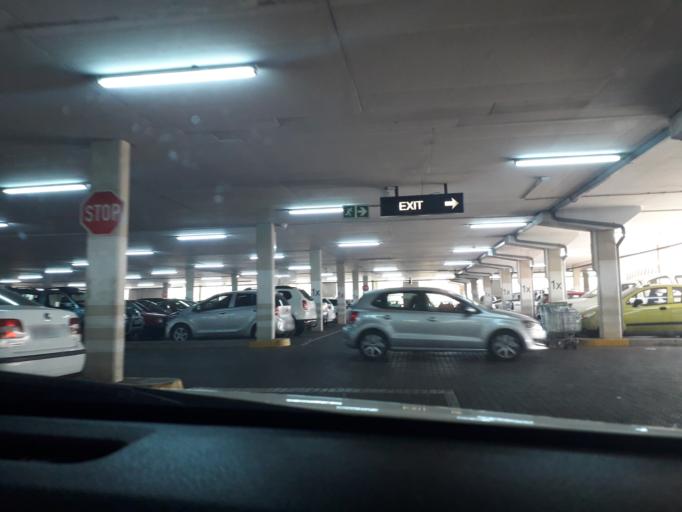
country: ZA
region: Gauteng
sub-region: City of Johannesburg Metropolitan Municipality
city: Modderfontein
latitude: -26.1029
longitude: 28.2219
